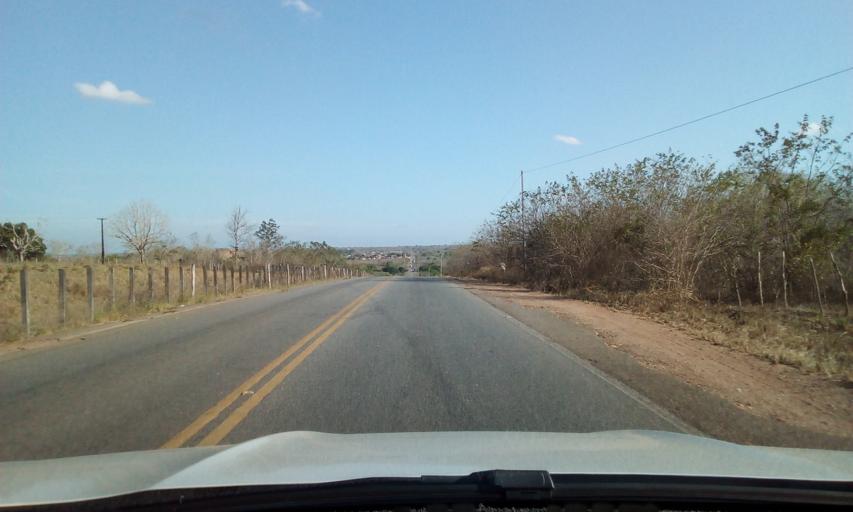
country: BR
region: Paraiba
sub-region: Mulungu
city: Mulungu
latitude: -6.9455
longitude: -35.4241
